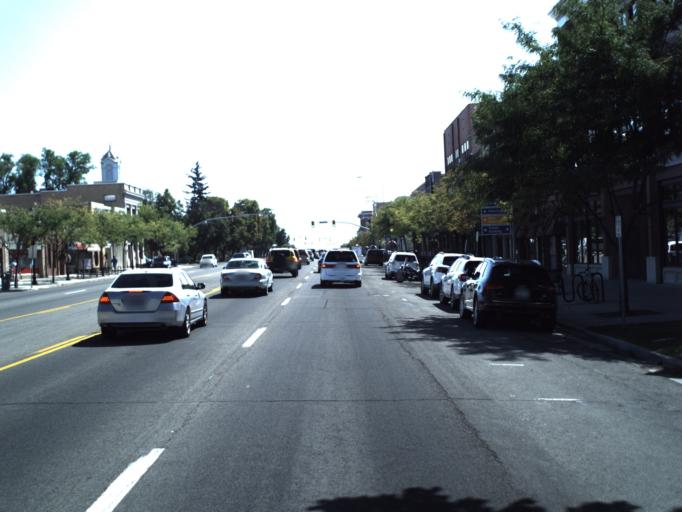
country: US
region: Utah
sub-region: Cache County
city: Logan
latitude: 41.7347
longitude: -111.8350
